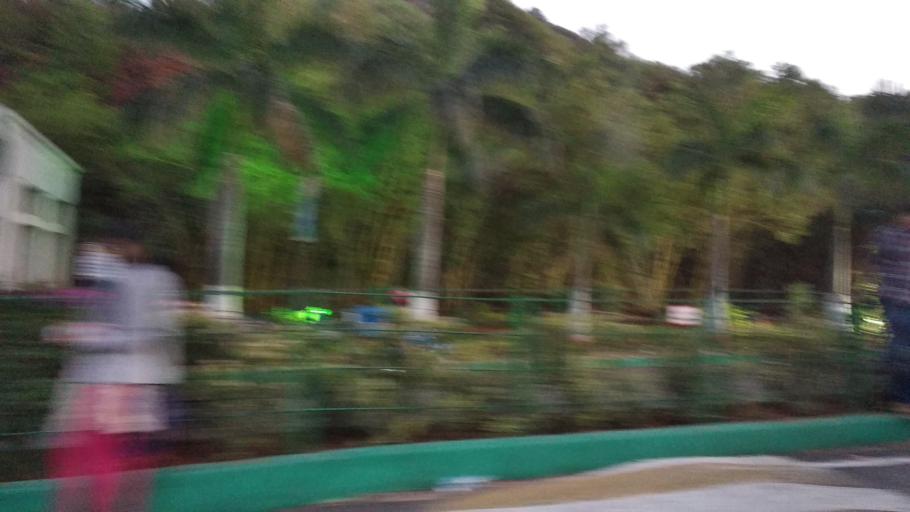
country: IN
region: Andhra Pradesh
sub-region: Vishakhapatnam
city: Bhimunipatnam
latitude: 17.7812
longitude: 83.3810
